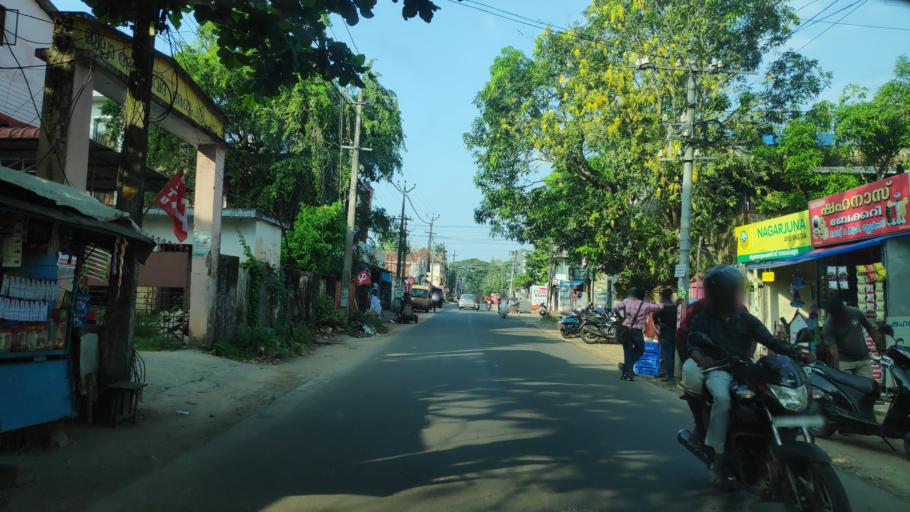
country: IN
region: Kerala
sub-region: Alappuzha
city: Alleppey
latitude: 9.4886
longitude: 76.3336
